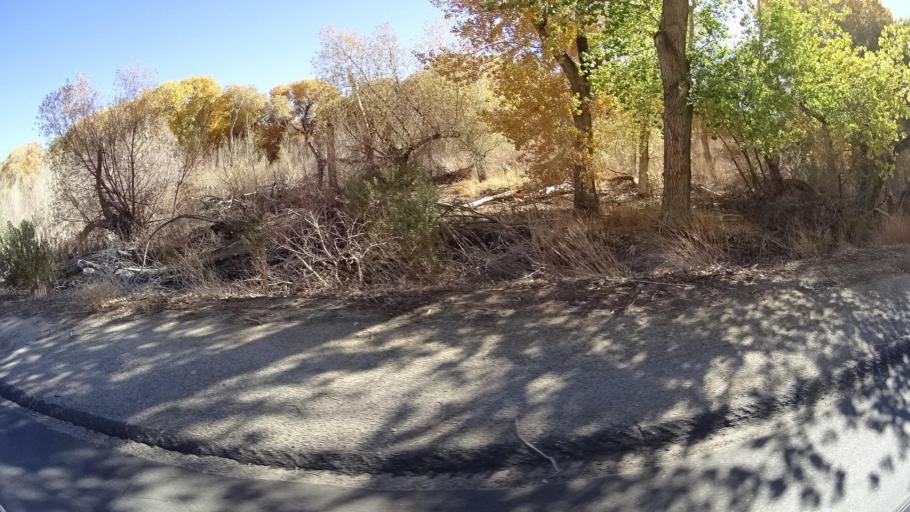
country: US
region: California
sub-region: Kern County
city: Weldon
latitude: 35.6723
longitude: -118.3335
